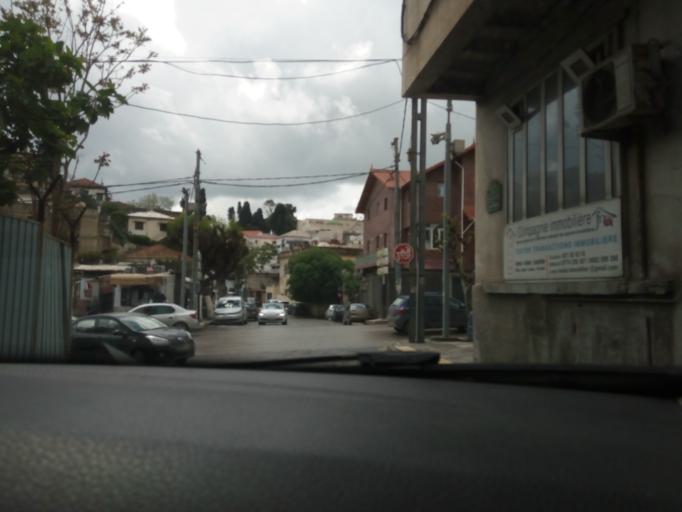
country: DZ
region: Alger
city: Algiers
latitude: 36.7669
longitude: 3.0359
